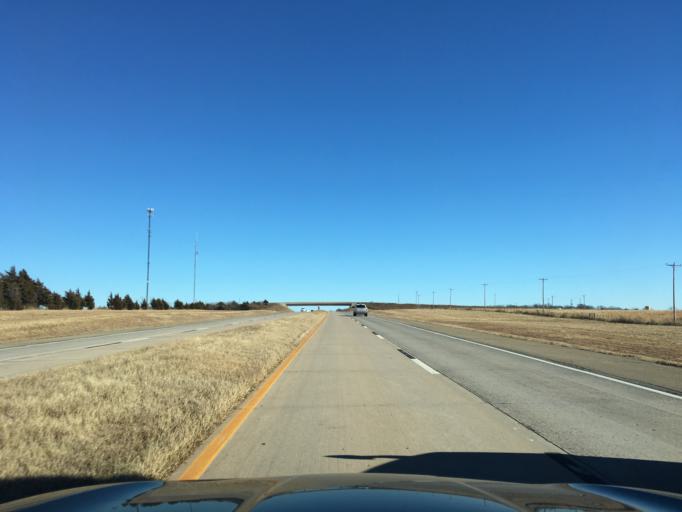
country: US
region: Oklahoma
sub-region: Payne County
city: Yale
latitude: 36.2242
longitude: -96.7531
